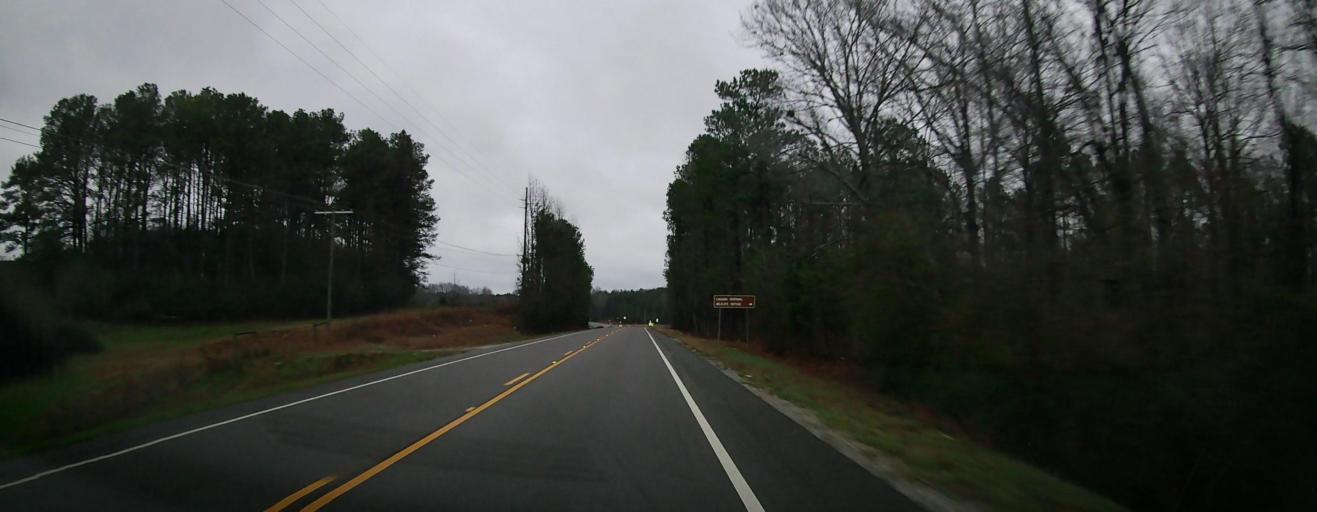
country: US
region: Alabama
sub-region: Bibb County
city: West Blocton
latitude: 33.1076
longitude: -87.1384
